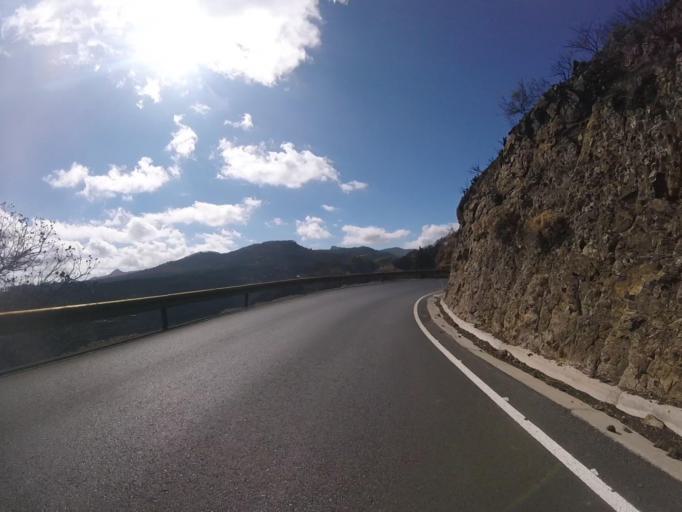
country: ES
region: Canary Islands
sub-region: Provincia de Las Palmas
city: Tejeda
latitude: 27.9956
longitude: -15.5944
